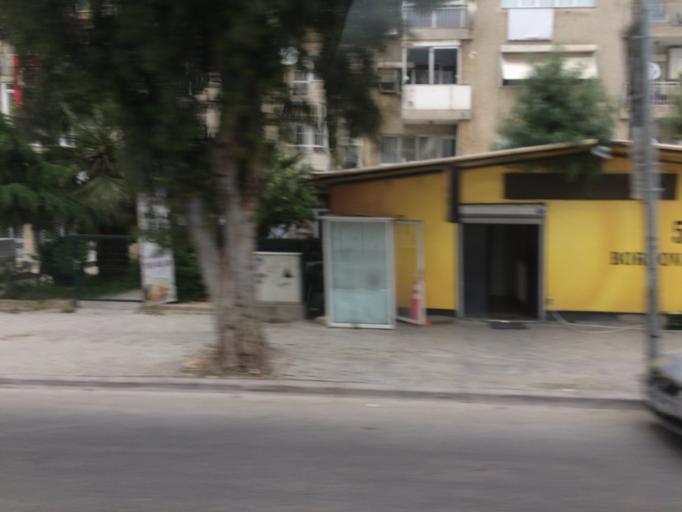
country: TR
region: Izmir
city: Bornova
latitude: 38.4575
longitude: 27.2051
